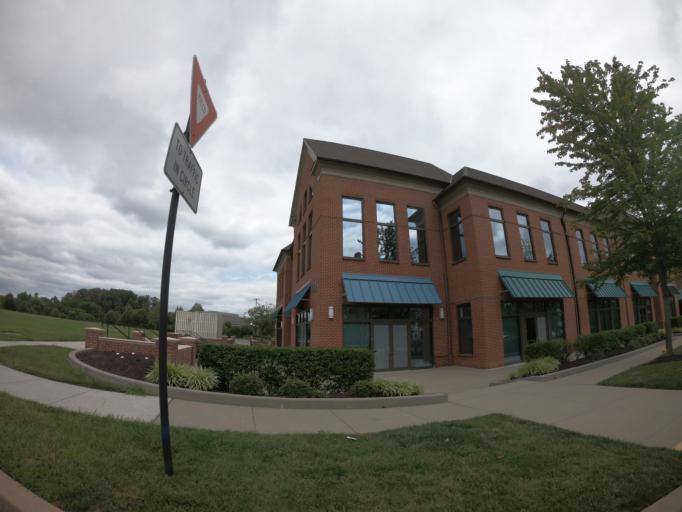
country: US
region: Maryland
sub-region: Howard County
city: Fulton
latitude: 39.1579
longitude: -76.9041
